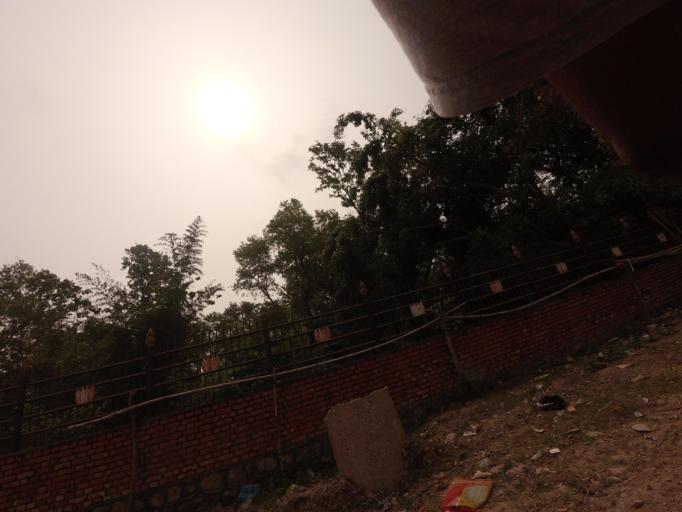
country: IN
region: Uttar Pradesh
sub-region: Maharajganj
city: Nautanwa
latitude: 27.4899
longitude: 83.2681
